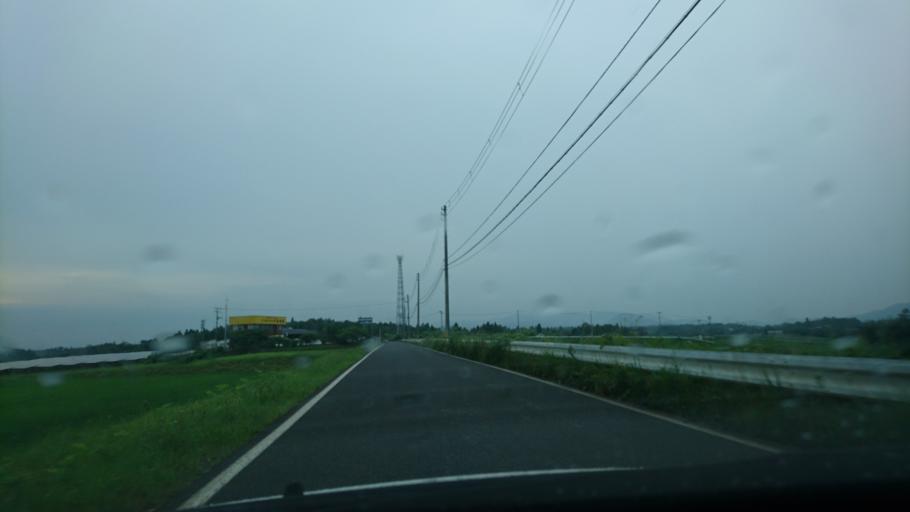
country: JP
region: Iwate
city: Ichinoseki
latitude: 38.9001
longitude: 141.1954
